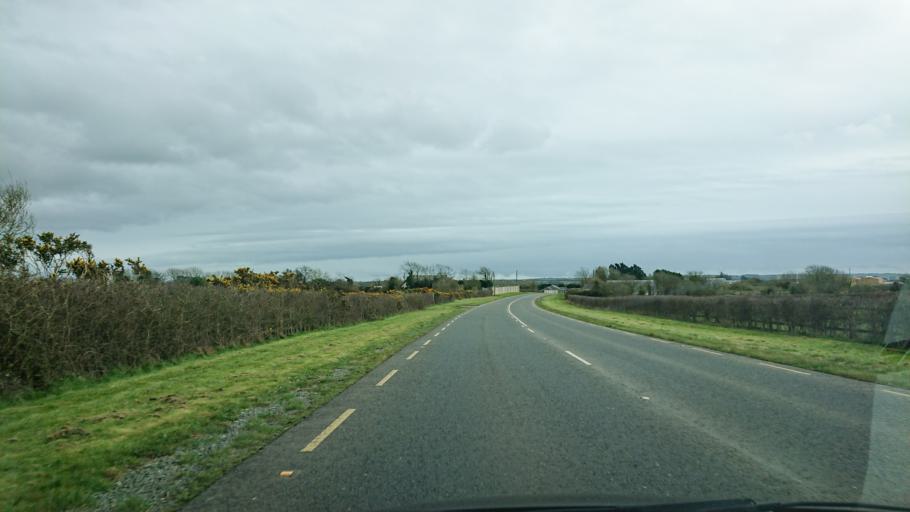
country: IE
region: Munster
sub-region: Waterford
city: Waterford
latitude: 52.1974
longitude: -7.0782
